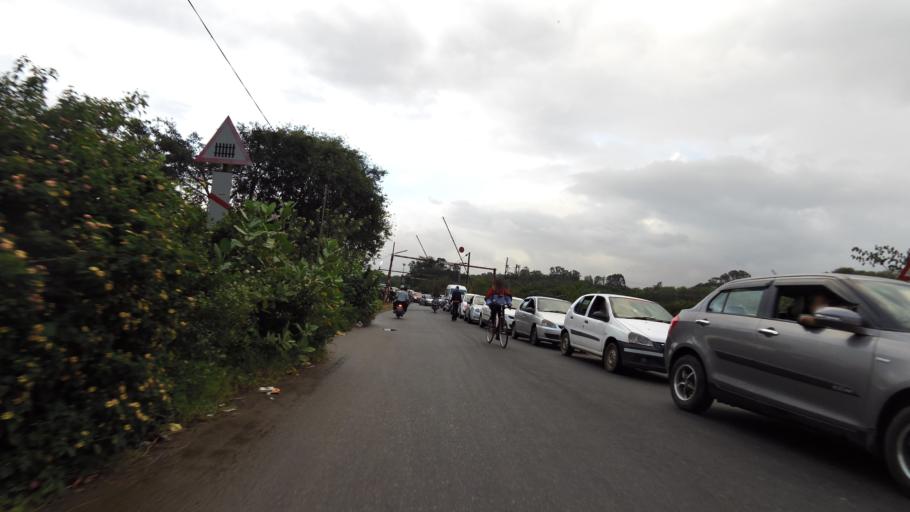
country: IN
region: Karnataka
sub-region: Bangalore Urban
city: Bangalore
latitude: 12.9922
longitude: 77.6452
